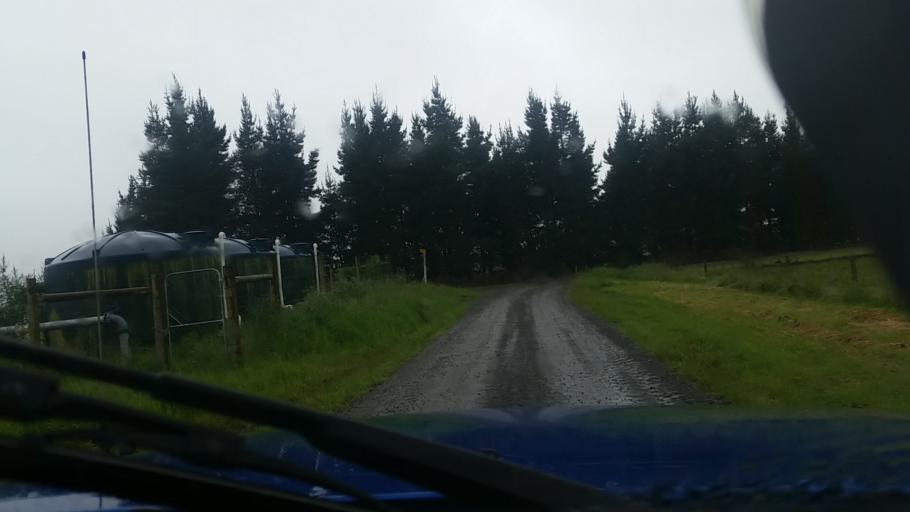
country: NZ
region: Canterbury
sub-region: Ashburton District
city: Methven
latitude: -43.5836
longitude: 171.5391
